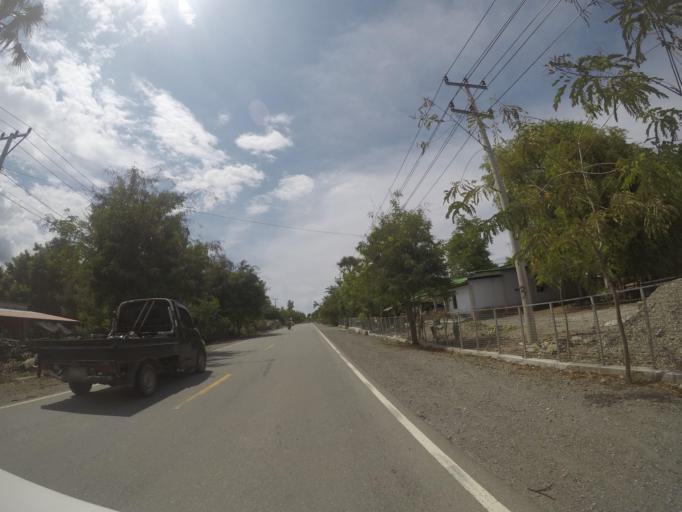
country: TL
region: Liquica
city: Liquica
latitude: -8.5656
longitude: 125.4213
